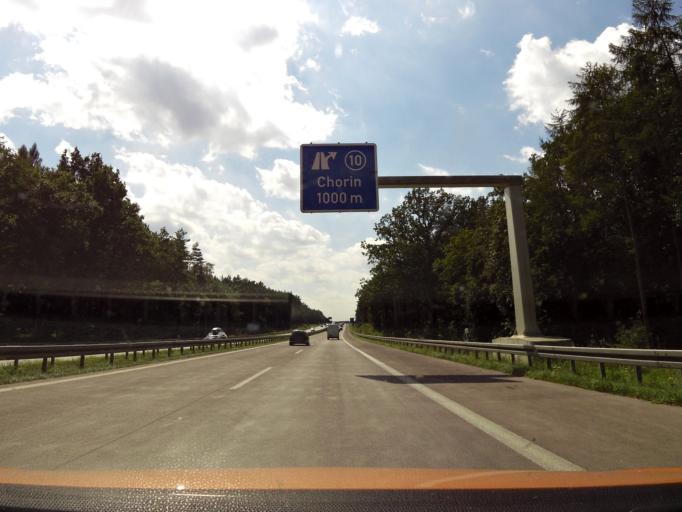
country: DE
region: Brandenburg
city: Althuttendorf
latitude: 52.9485
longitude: 13.8029
